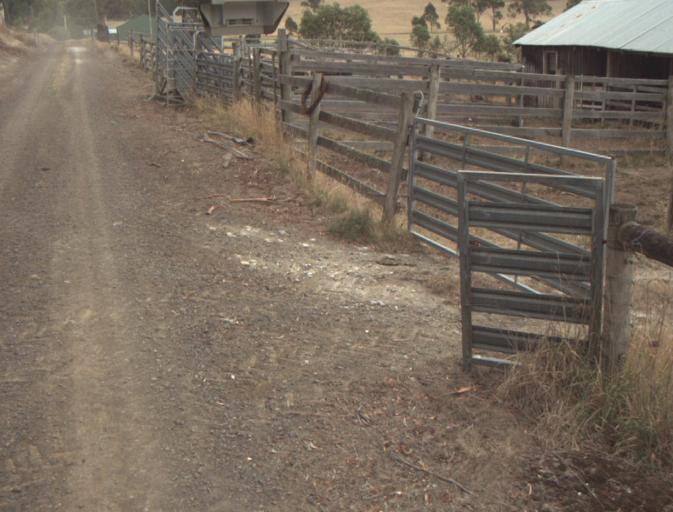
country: AU
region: Tasmania
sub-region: Launceston
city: Mayfield
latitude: -41.2394
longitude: 147.1861
